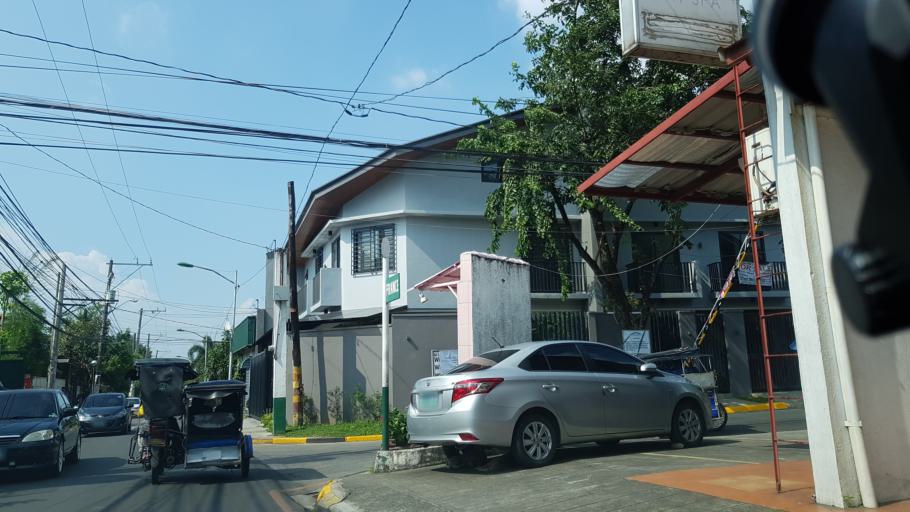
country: PH
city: Sambayanihan People's Village
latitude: 14.4790
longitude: 121.0308
